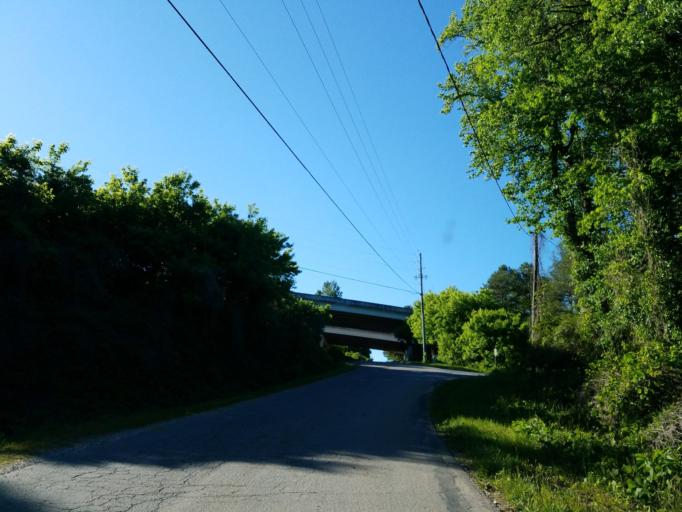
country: US
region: Georgia
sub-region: Gilmer County
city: Ellijay
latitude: 34.6396
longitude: -84.4982
